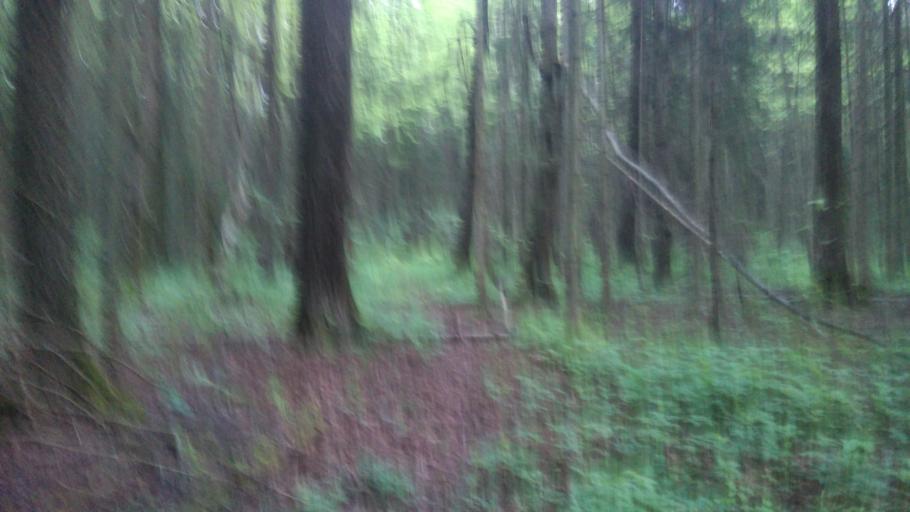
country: RU
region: Perm
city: Froly
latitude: 57.9617
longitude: 56.3042
